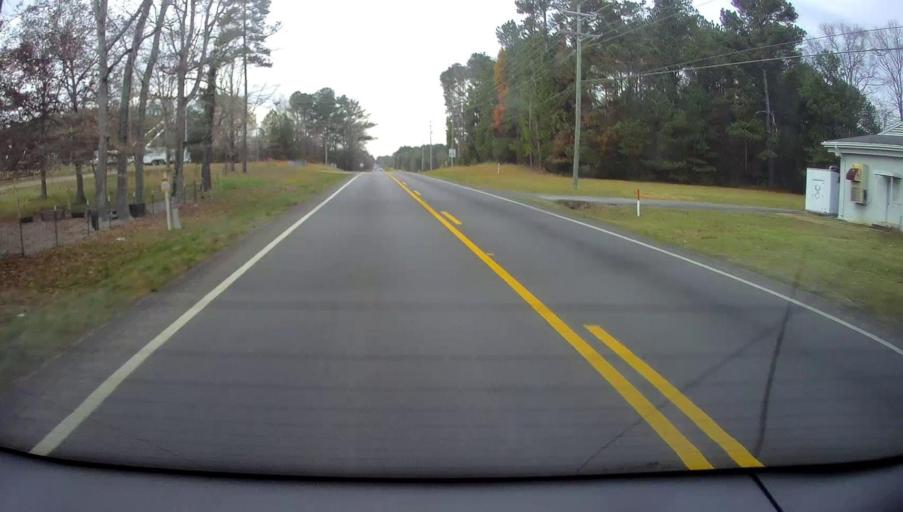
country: US
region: Alabama
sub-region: Morgan County
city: Priceville
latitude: 34.4492
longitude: -86.7611
